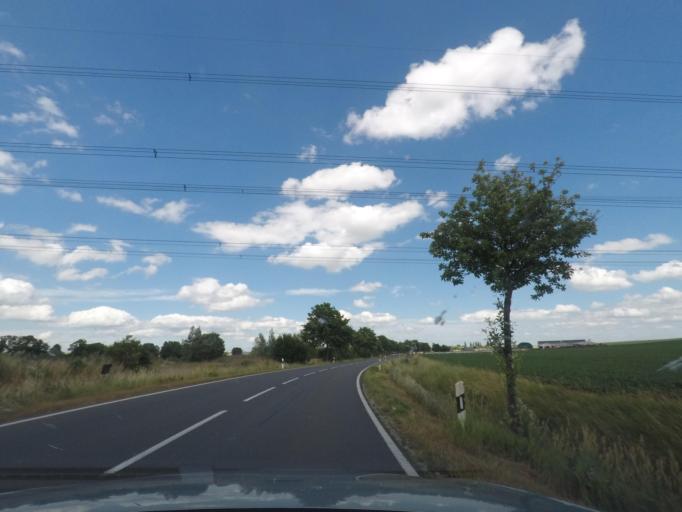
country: DE
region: Saxony-Anhalt
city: Gross Quenstedt
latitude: 51.9182
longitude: 11.1017
